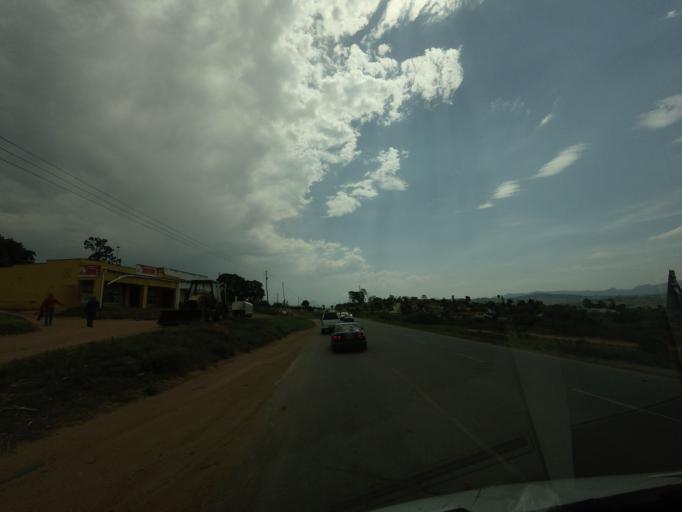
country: SZ
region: Manzini
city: Manzini
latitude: -26.4926
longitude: 31.4082
